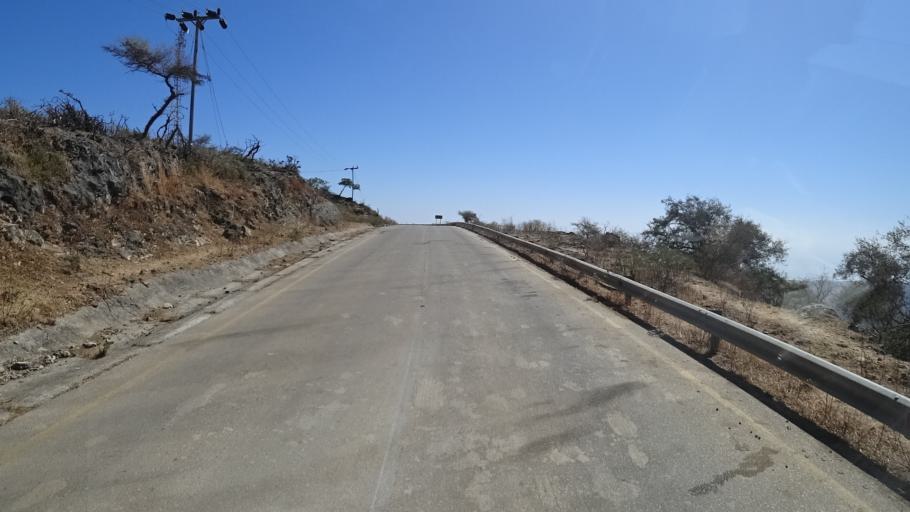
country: YE
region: Al Mahrah
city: Hawf
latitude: 16.7712
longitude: 53.3352
